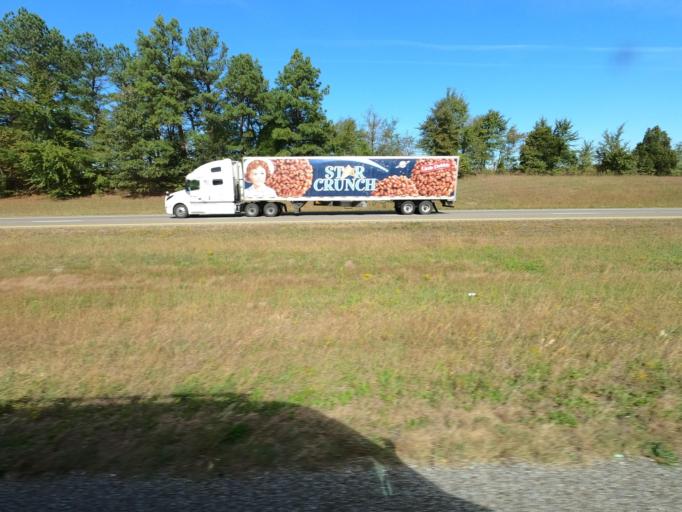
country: US
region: Tennessee
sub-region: Haywood County
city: Brownsville
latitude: 35.5677
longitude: -89.1522
